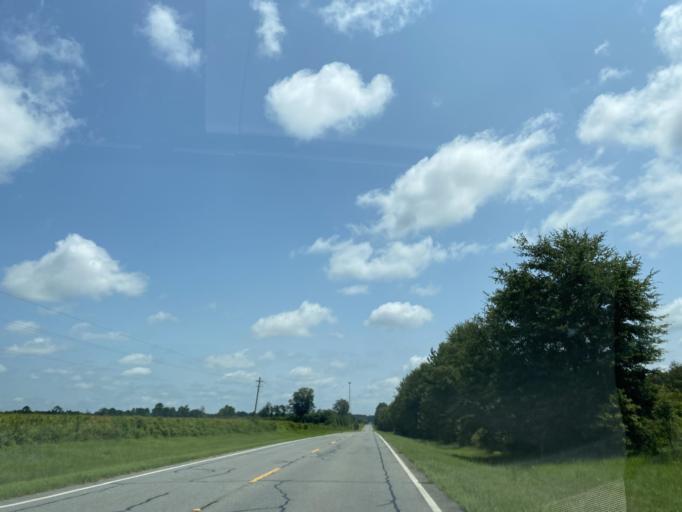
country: US
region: Georgia
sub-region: Wilcox County
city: Abbeville
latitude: 31.9961
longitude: -83.1849
